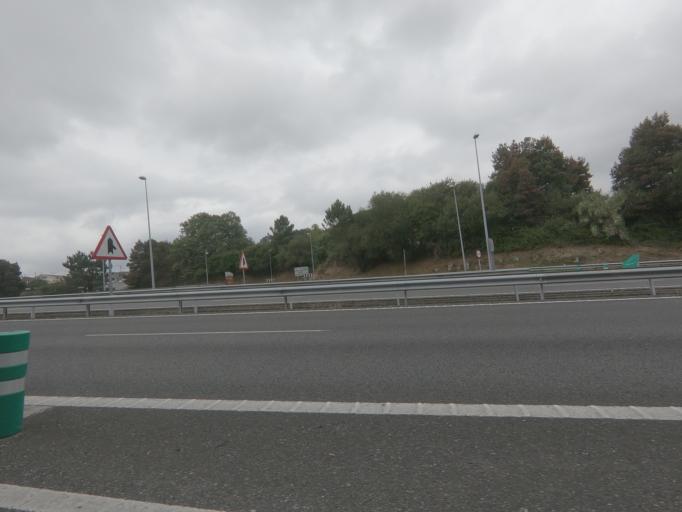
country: ES
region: Galicia
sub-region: Provincia de Pontevedra
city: Tui
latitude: 42.0524
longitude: -8.6550
